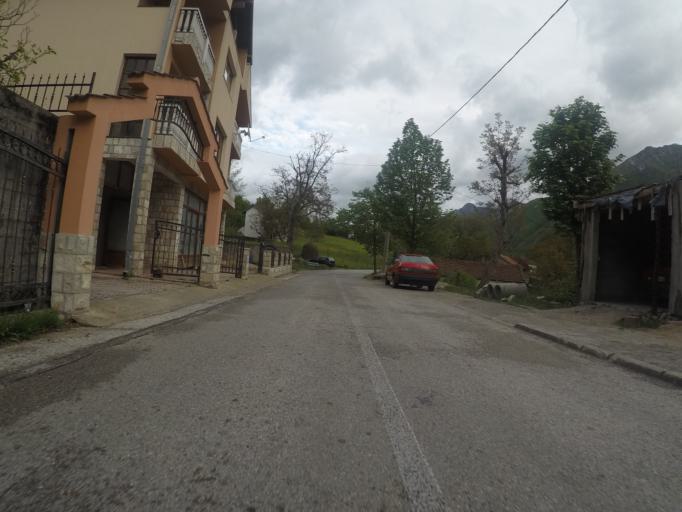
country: BA
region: Federation of Bosnia and Herzegovina
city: Siroki Brijeg
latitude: 43.5414
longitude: 17.5822
